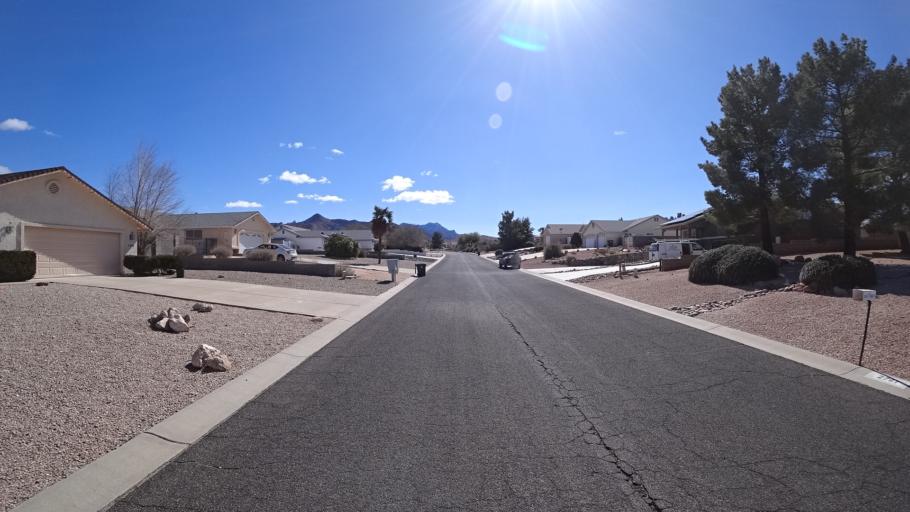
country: US
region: Arizona
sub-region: Mohave County
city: Kingman
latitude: 35.2030
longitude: -113.9651
